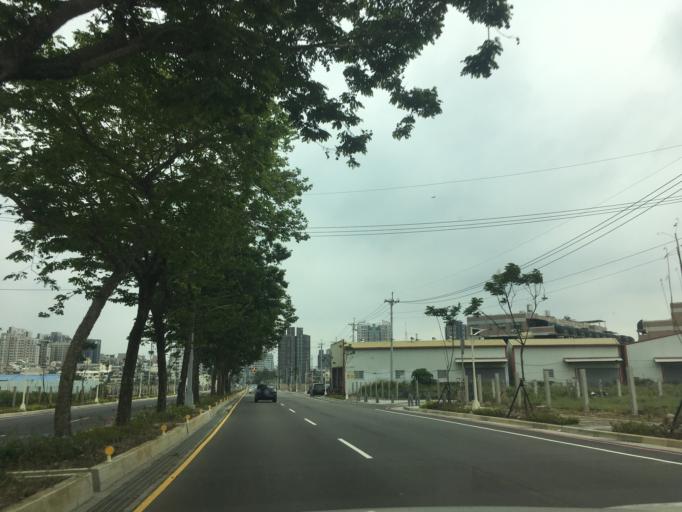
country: TW
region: Taiwan
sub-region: Taichung City
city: Taichung
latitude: 24.1824
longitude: 120.6769
